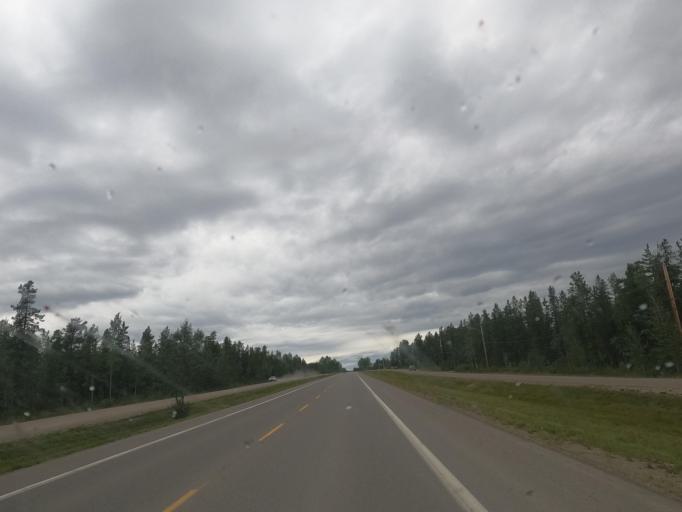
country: CA
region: Yukon
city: Watson Lake
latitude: 60.0538
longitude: -128.6679
